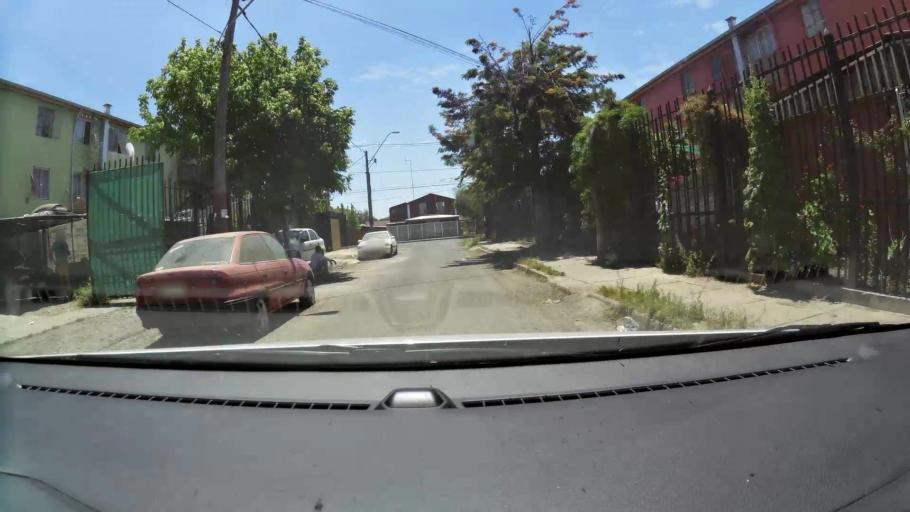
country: CL
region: Santiago Metropolitan
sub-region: Provincia de Santiago
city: La Pintana
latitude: -33.5582
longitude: -70.6210
